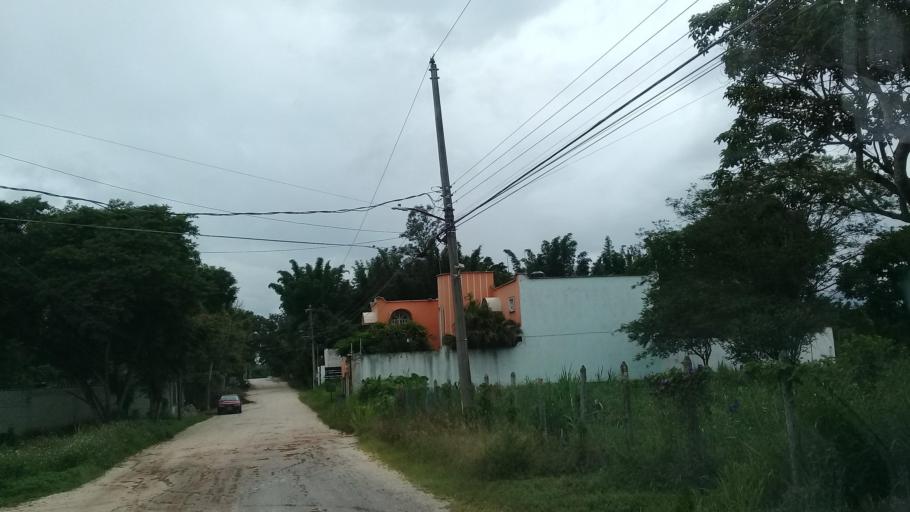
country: MX
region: Veracruz
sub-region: Emiliano Zapata
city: Jacarandas
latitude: 19.5058
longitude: -96.8400
